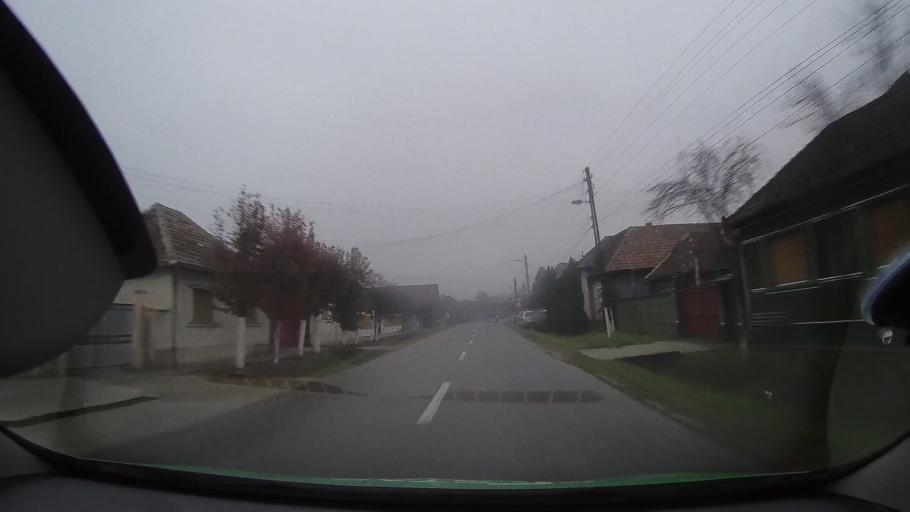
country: RO
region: Bihor
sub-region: Comuna Tulca
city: Tulca
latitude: 46.7874
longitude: 21.7809
